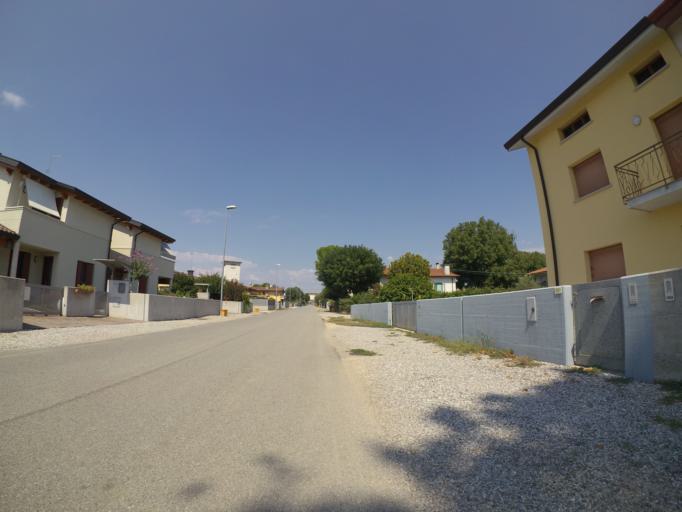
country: IT
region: Friuli Venezia Giulia
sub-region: Provincia di Udine
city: Codroipo
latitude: 45.9527
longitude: 12.9862
